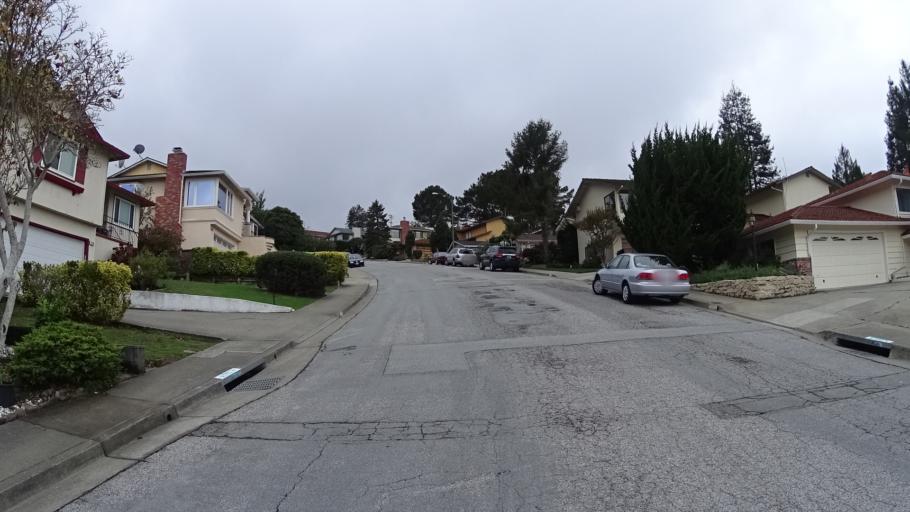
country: US
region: California
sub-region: San Mateo County
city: Millbrae
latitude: 37.5965
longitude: -122.4146
